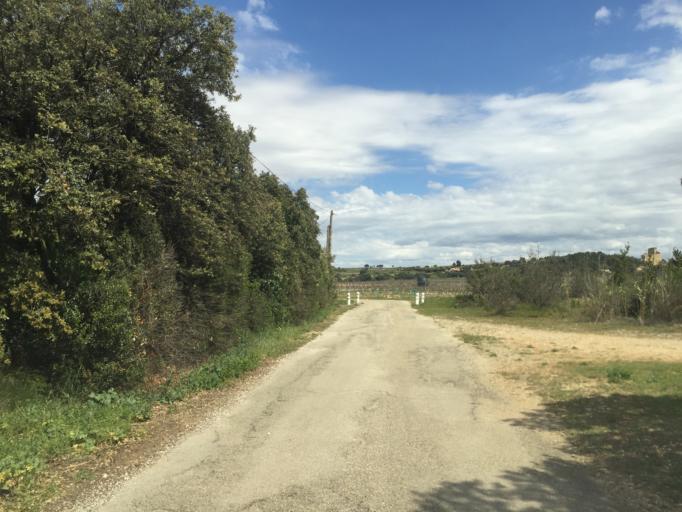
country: FR
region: Provence-Alpes-Cote d'Azur
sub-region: Departement du Vaucluse
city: Chateauneuf-du-Pape
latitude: 44.0539
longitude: 4.8139
